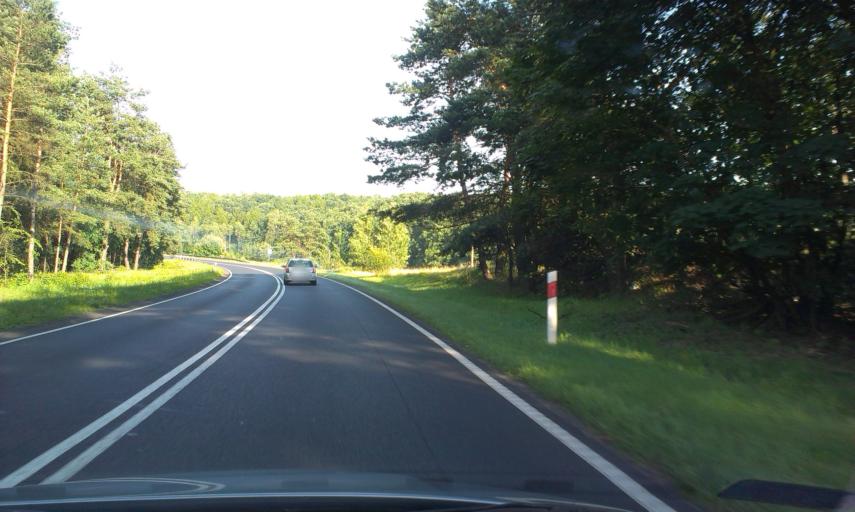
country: PL
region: Kujawsko-Pomorskie
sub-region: Powiat bydgoski
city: Sicienko
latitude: 53.1604
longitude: 17.7939
